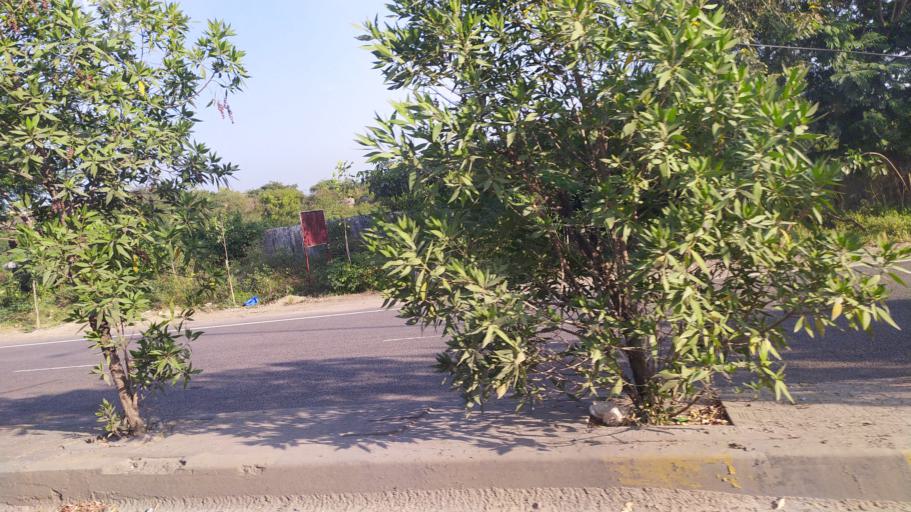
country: IN
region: Telangana
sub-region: Hyderabad
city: Hyderabad
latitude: 17.3201
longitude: 78.3886
